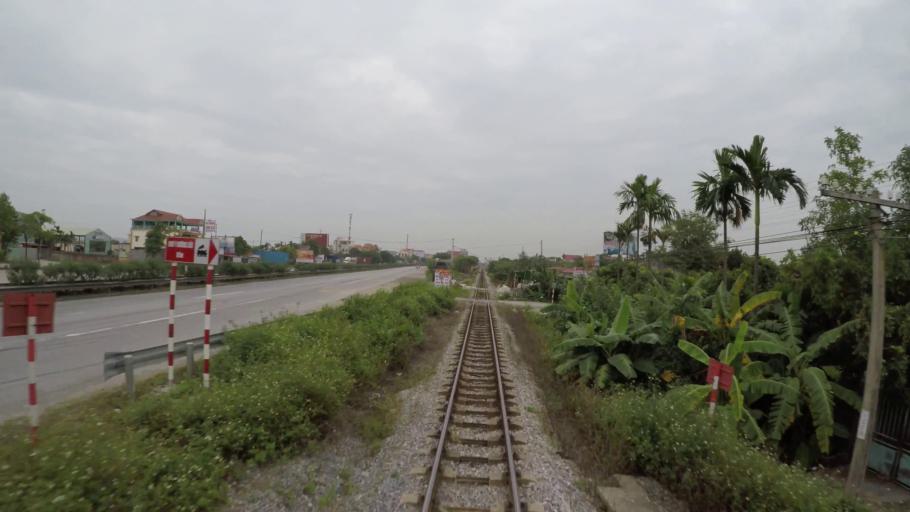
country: VN
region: Hai Duong
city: Phu Thai
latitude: 20.9746
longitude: 106.4359
